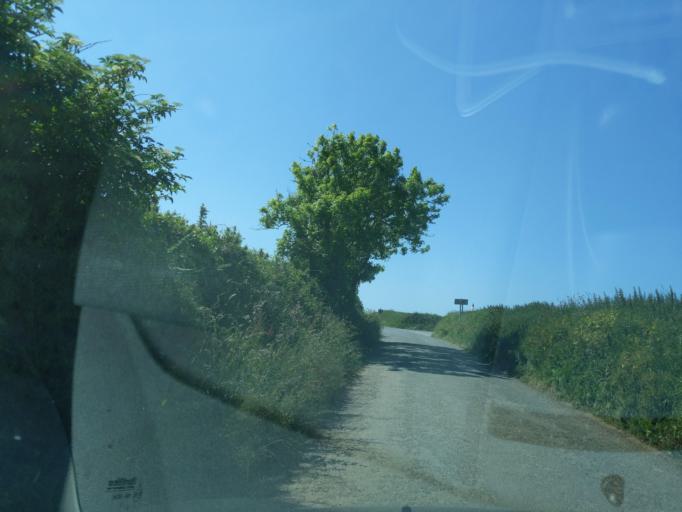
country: GB
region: England
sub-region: Cornwall
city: Wadebridge
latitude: 50.5809
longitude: -4.8346
